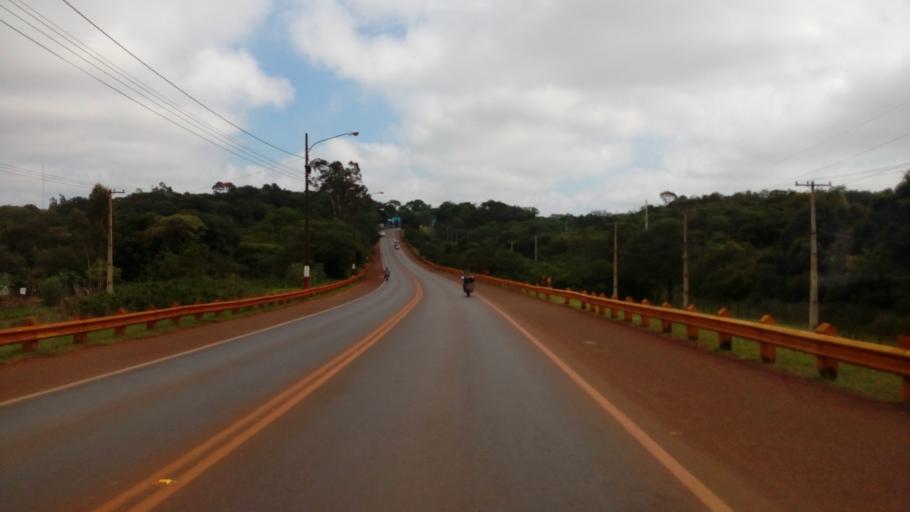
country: PY
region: Alto Parana
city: Ciudad del Este
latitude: -25.4181
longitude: -54.6361
